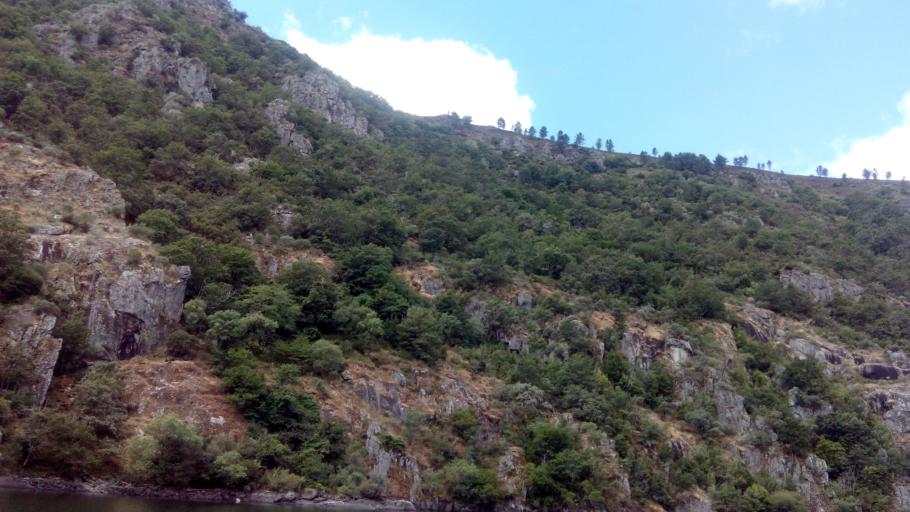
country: ES
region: Galicia
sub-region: Provincia de Lugo
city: Sober
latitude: 42.3953
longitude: -7.6271
